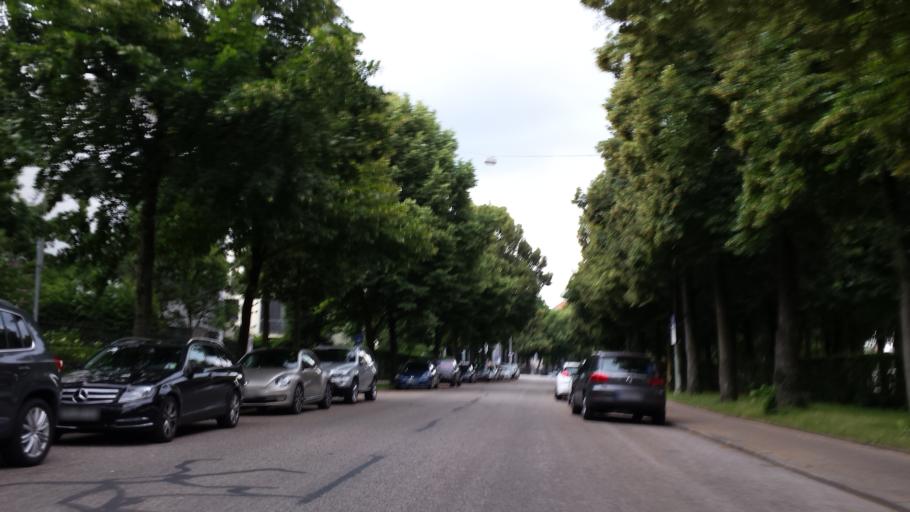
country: DE
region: Bavaria
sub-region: Upper Bavaria
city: Munich
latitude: 48.1314
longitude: 11.5536
